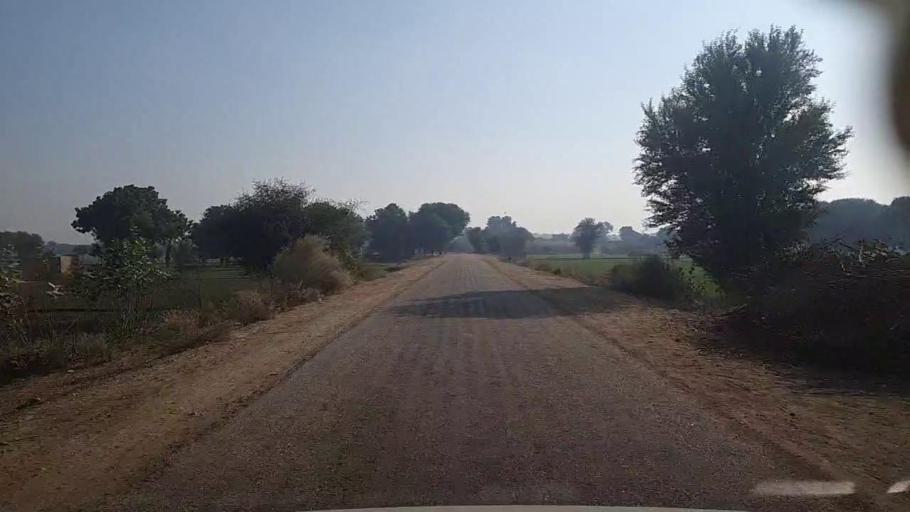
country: PK
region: Sindh
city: Kandiari
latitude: 26.8176
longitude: 68.4952
